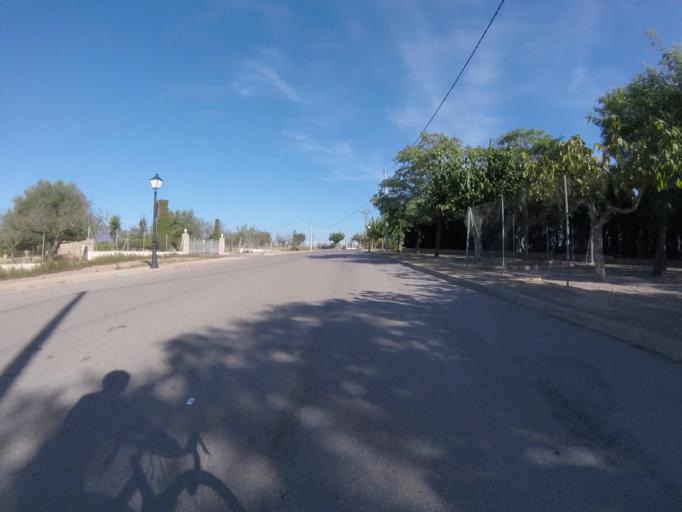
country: ES
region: Valencia
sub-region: Provincia de Castello
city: Benlloch
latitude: 40.2335
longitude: 0.0766
